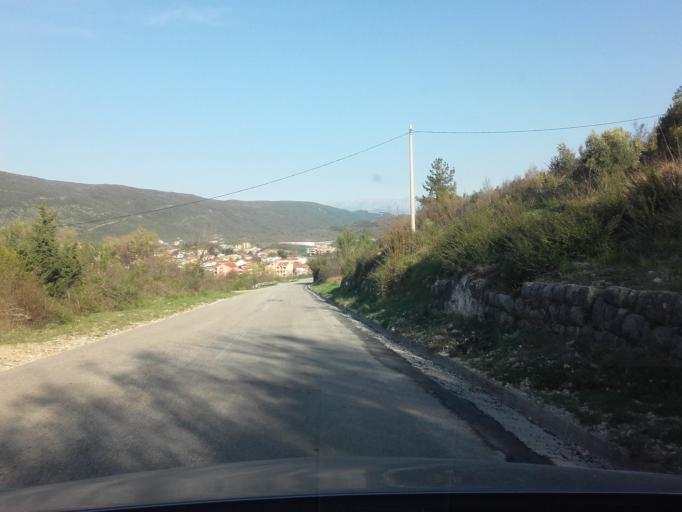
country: ME
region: Budva
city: Budva
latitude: 42.3038
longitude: 18.8087
